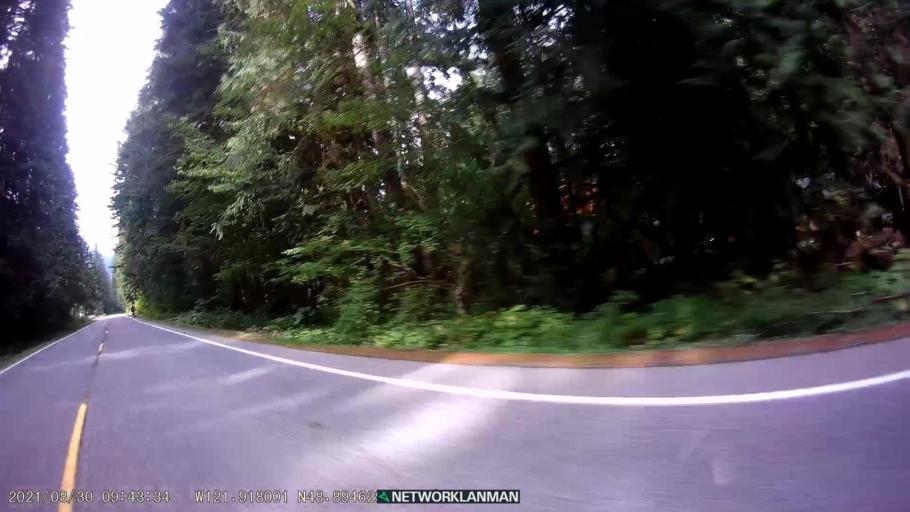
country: US
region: Washington
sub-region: Whatcom County
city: Peaceful Valley
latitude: 48.8876
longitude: -121.9281
